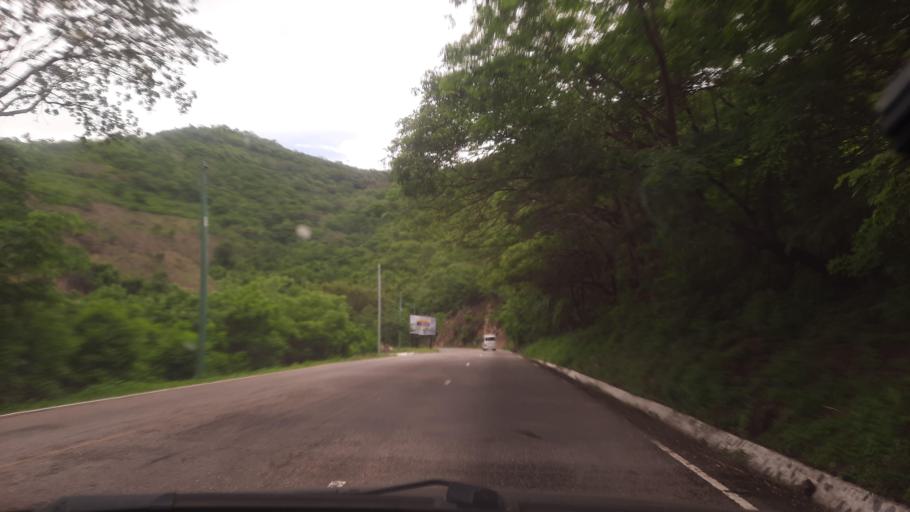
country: GT
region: Chiquimula
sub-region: Municipio de Chiquimula
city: Chiquimula
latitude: 14.8787
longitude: -89.5160
